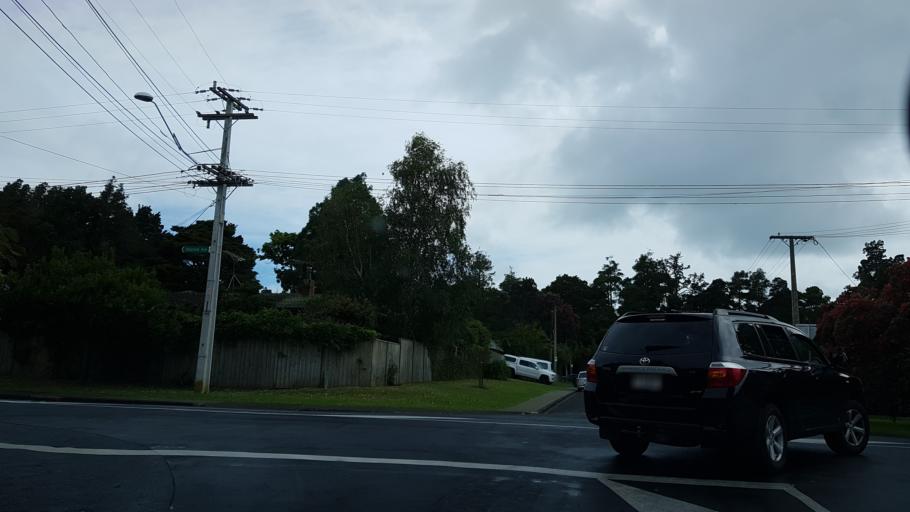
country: NZ
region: Auckland
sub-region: Auckland
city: North Shore
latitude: -36.7930
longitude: 174.7420
